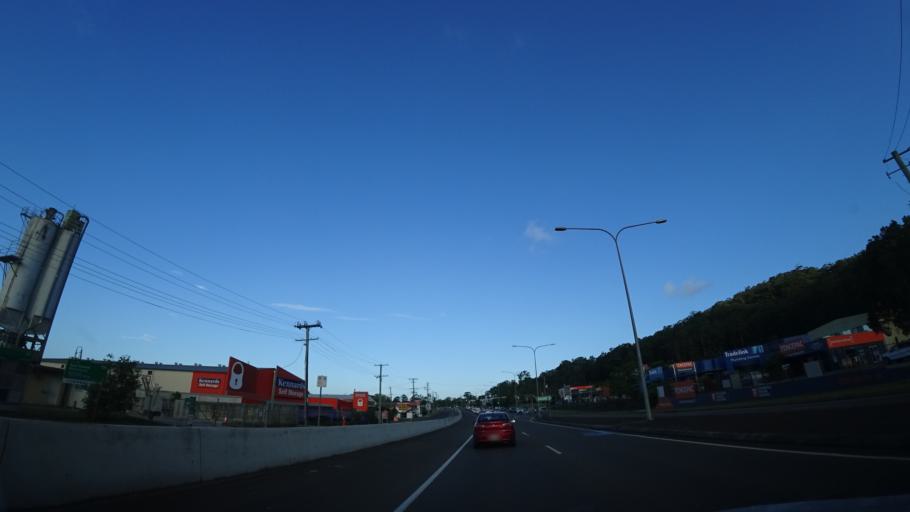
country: AU
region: Queensland
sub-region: Sunshine Coast
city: Buderim
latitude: -26.6630
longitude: 153.0399
